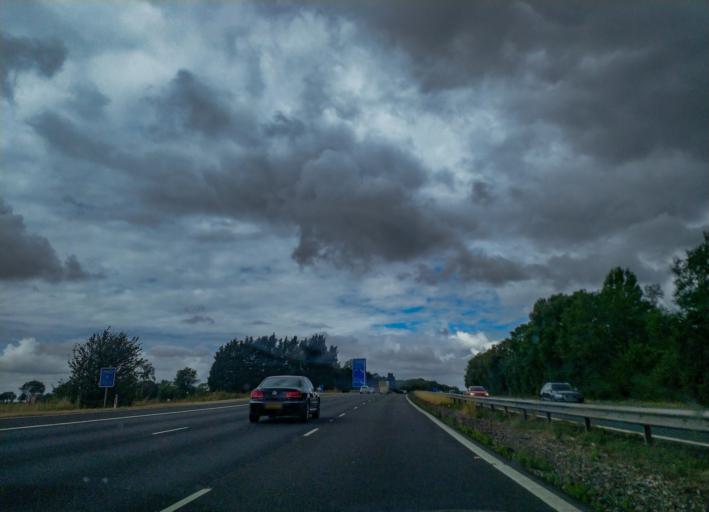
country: GB
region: England
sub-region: Oxfordshire
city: Chalgrove
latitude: 51.7221
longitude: -1.0484
